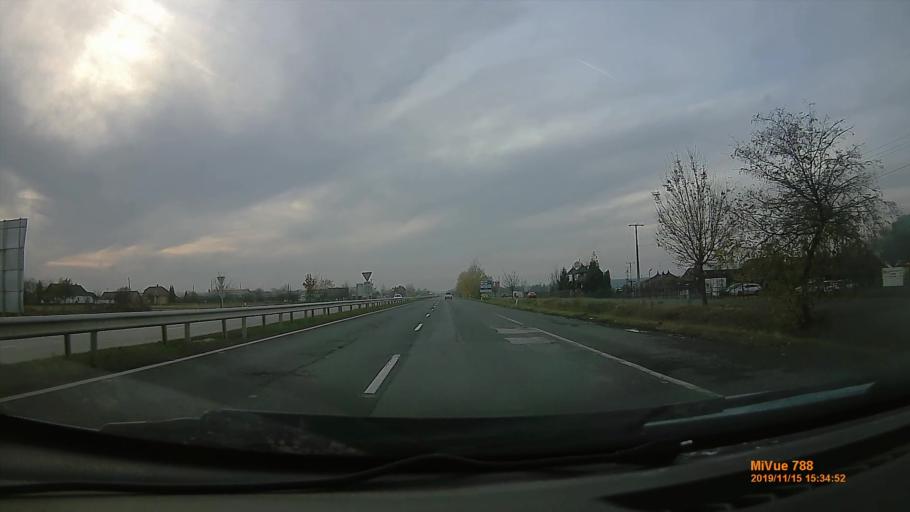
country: HU
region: Bekes
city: Gyula
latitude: 46.6531
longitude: 21.2365
